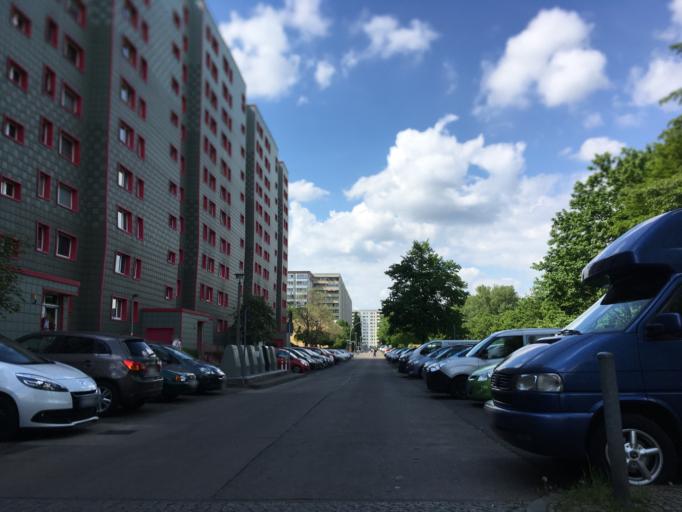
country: DE
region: Berlin
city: Neu-Hohenschoenhausen
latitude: 52.5687
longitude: 13.5052
